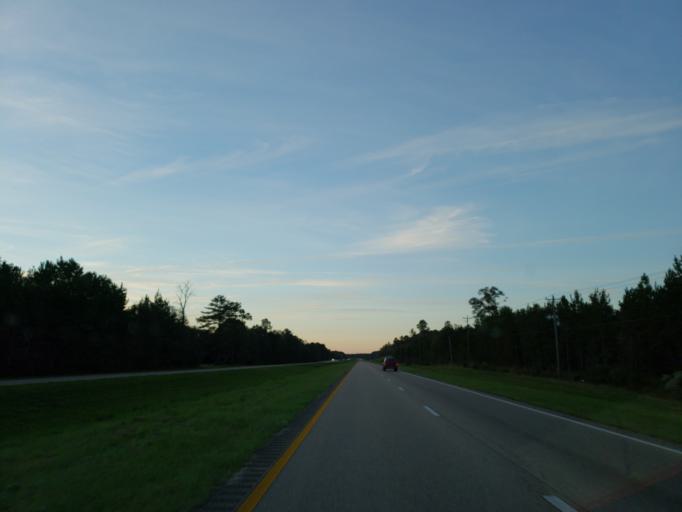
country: US
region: Mississippi
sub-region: Wayne County
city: Belmont
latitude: 31.5849
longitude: -88.5449
